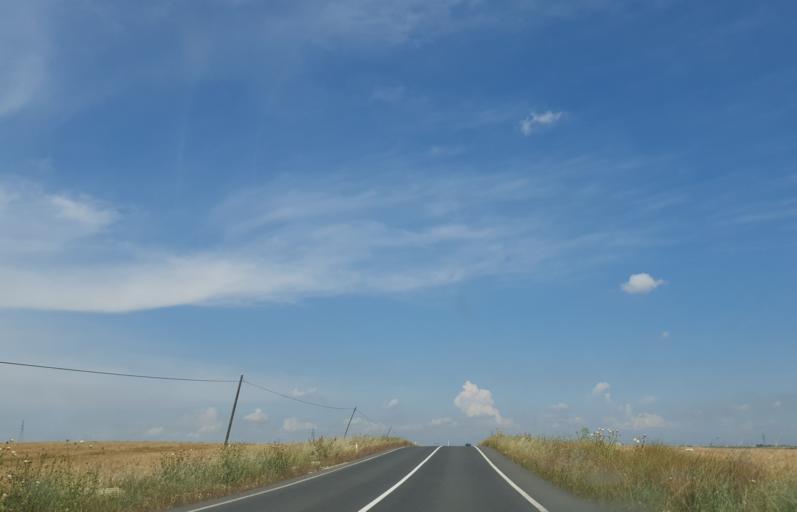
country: TR
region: Kirklareli
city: Buyukkaristiran
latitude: 41.2478
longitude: 27.6112
